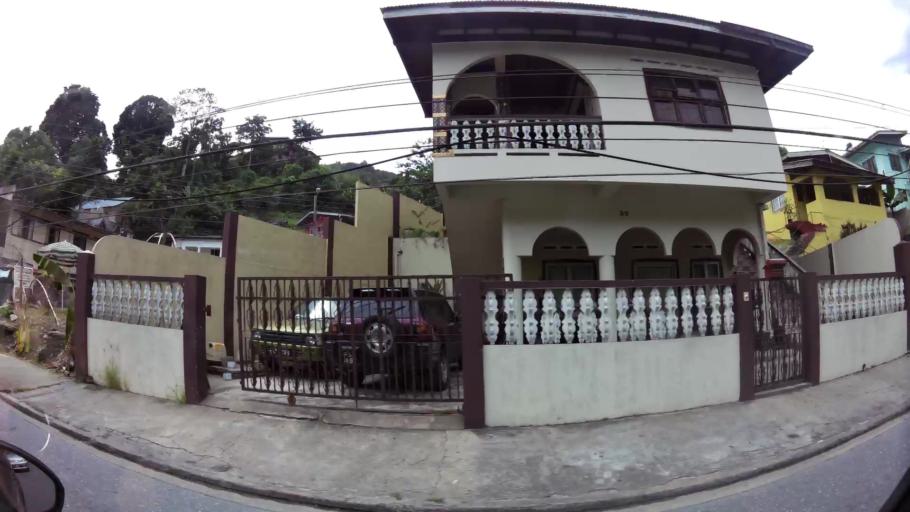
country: TT
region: Diego Martin
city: Petit Valley
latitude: 10.7101
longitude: -61.5141
